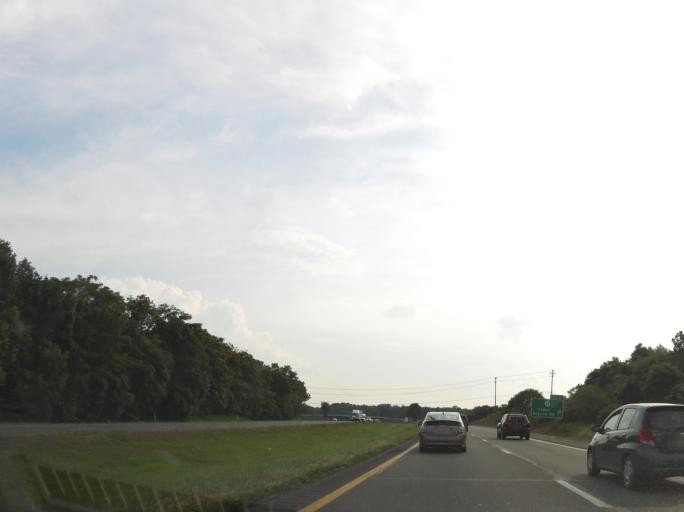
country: US
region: West Virginia
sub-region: Berkeley County
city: Inwood
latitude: 39.4110
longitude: -78.0194
